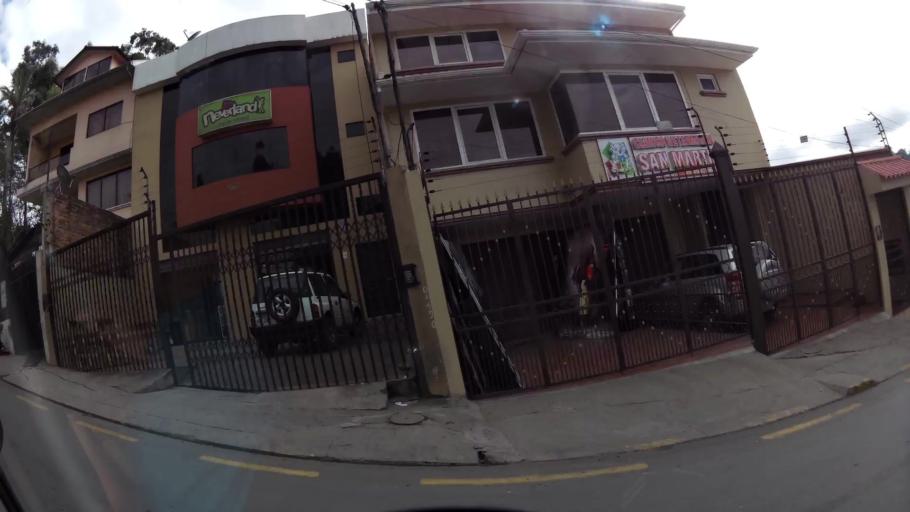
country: EC
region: Azuay
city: Cuenca
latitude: -2.8931
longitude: -78.9758
